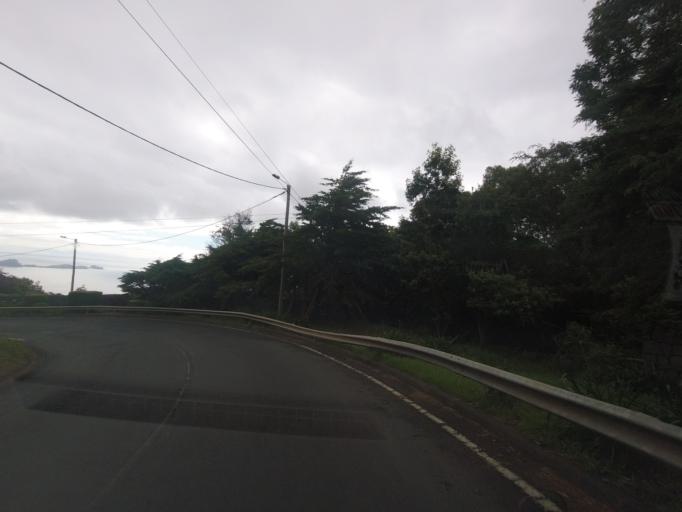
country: PT
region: Madeira
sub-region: Machico
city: Machico
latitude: 32.7066
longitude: -16.7875
